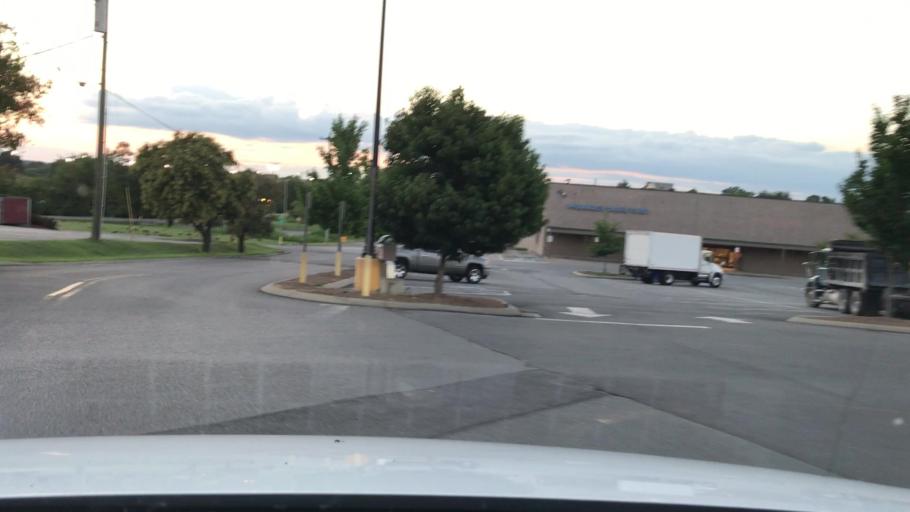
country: US
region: Tennessee
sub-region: Sumner County
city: Hendersonville
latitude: 36.3075
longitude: -86.6073
